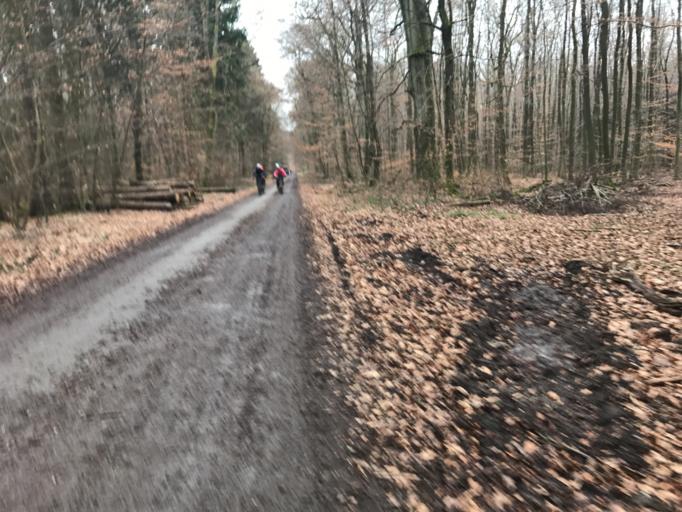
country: DE
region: Hesse
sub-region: Regierungsbezirk Darmstadt
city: Wiesbaden
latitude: 50.1212
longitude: 8.2399
